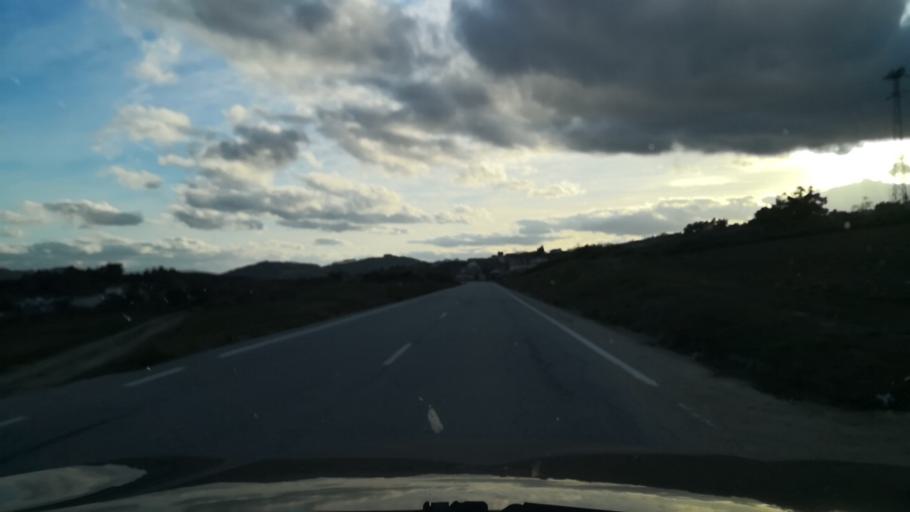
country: PT
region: Braganca
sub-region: Carrazeda de Ansiaes
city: Carrazeda de Anciaes
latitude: 41.2393
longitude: -7.3209
